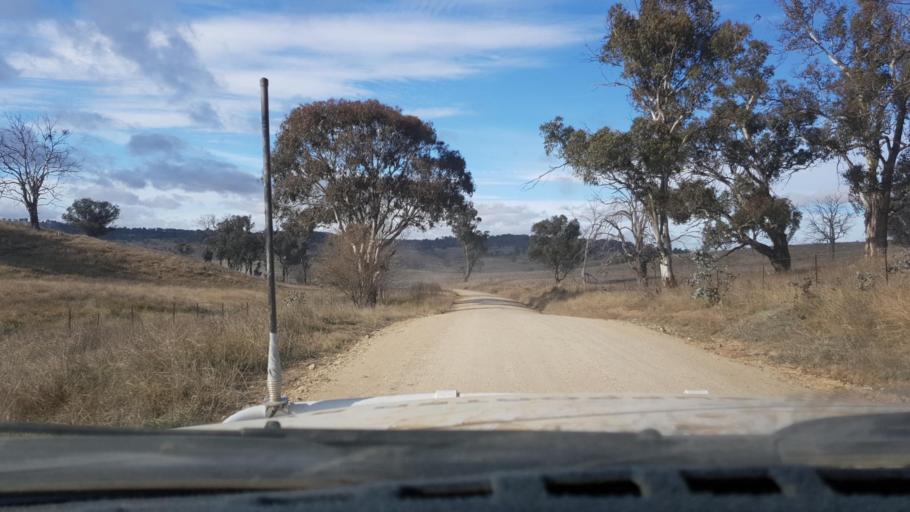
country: AU
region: New South Wales
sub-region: Armidale Dumaresq
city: Enmore
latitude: -30.7608
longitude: 151.6317
